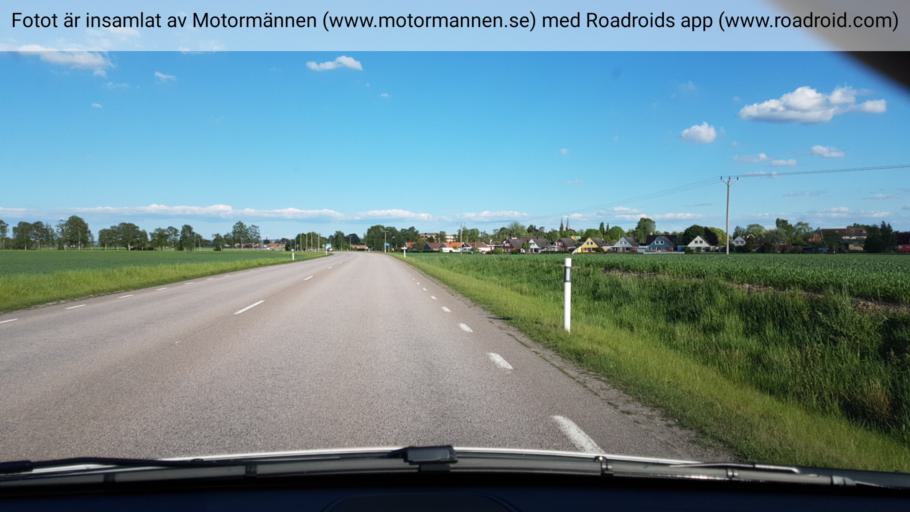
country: SE
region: Vaestra Goetaland
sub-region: Skara Kommun
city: Skara
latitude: 58.3949
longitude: 13.4182
